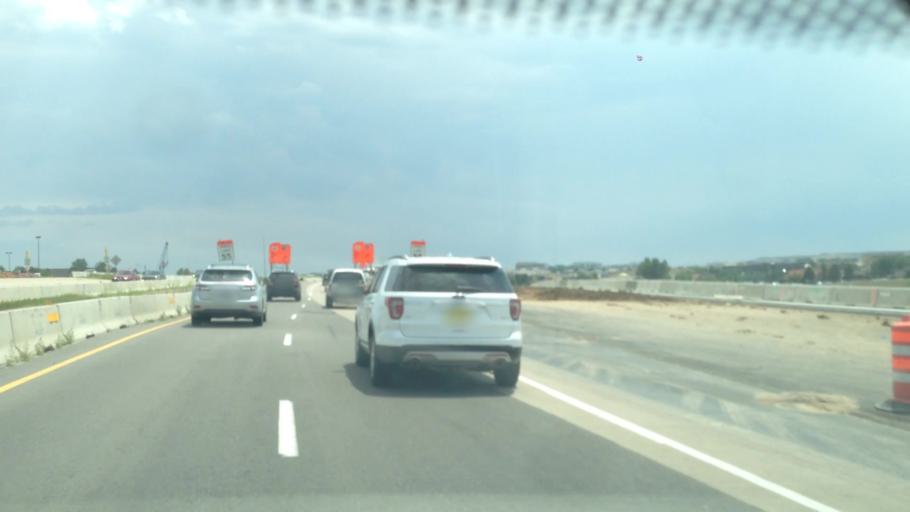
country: US
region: Colorado
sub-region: Adams County
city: Lone Tree
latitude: 39.5612
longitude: -104.8842
